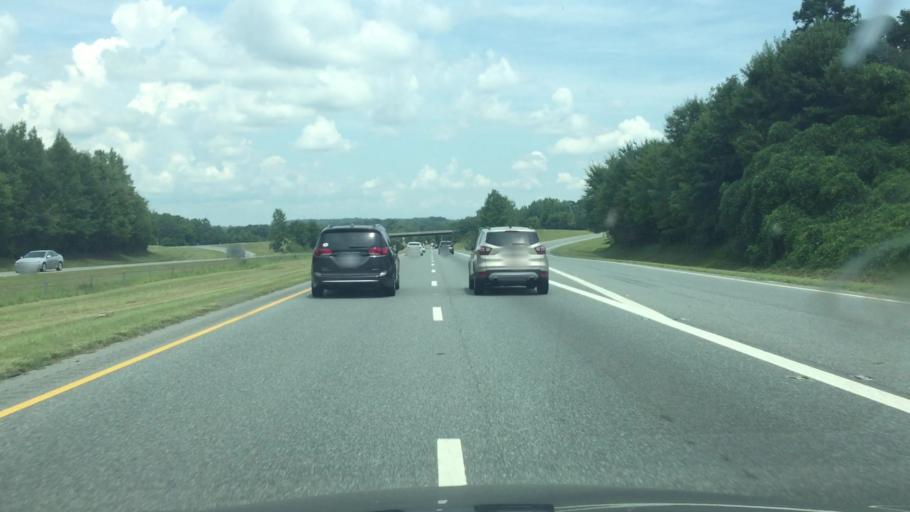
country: US
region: North Carolina
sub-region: Montgomery County
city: Biscoe
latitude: 35.4849
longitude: -79.7810
